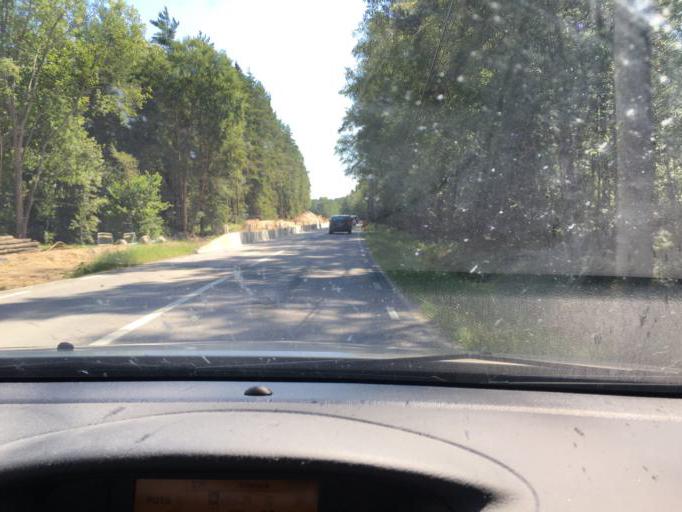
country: SE
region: Stockholm
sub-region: Varmdo Kommun
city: Mortnas
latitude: 59.2767
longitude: 18.4535
